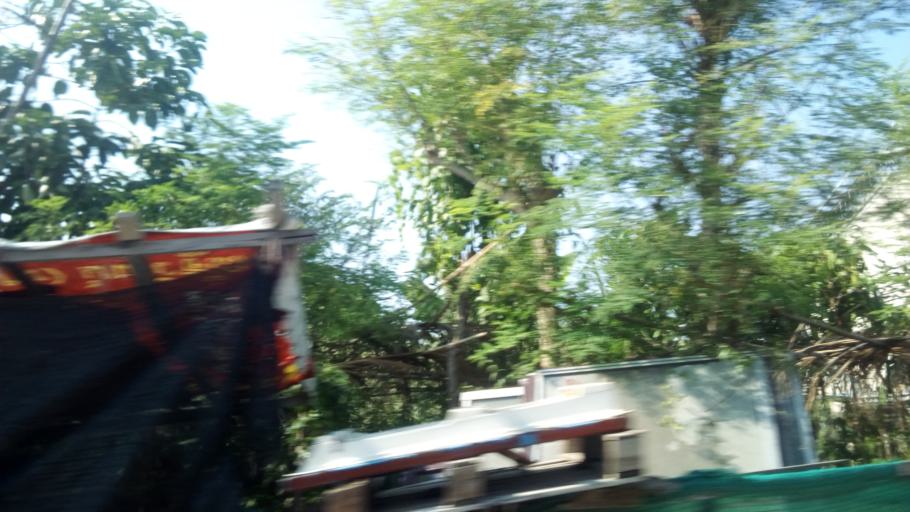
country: TH
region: Nakhon Pathom
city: Salaya
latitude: 13.8245
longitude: 100.3110
